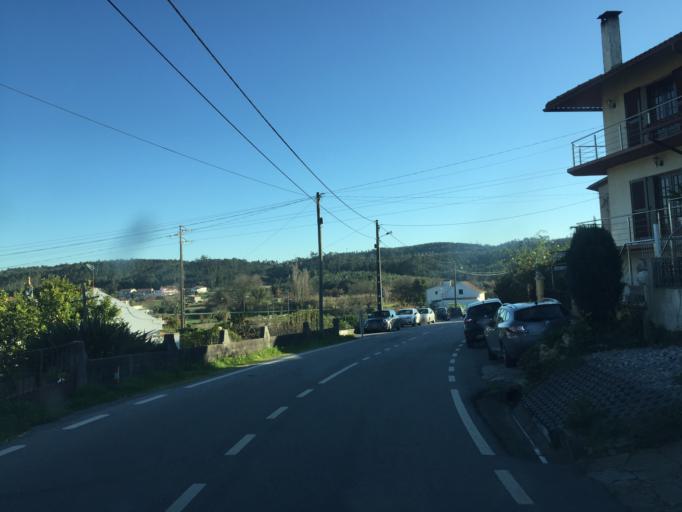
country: PT
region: Coimbra
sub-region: Figueira da Foz
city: Tavarede
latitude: 40.1645
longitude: -8.8183
